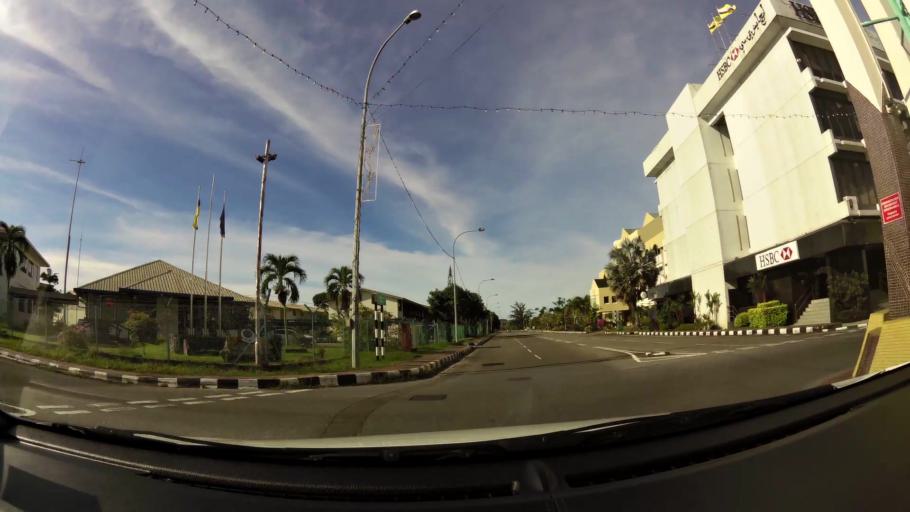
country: BN
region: Belait
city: Kuala Belait
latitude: 4.5843
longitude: 114.1916
